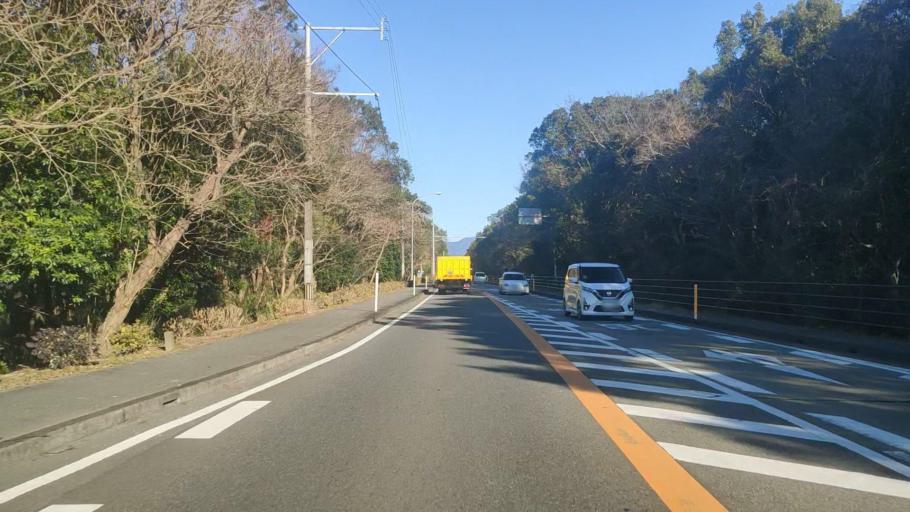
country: JP
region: Miyazaki
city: Nobeoka
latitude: 32.5297
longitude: 131.6815
